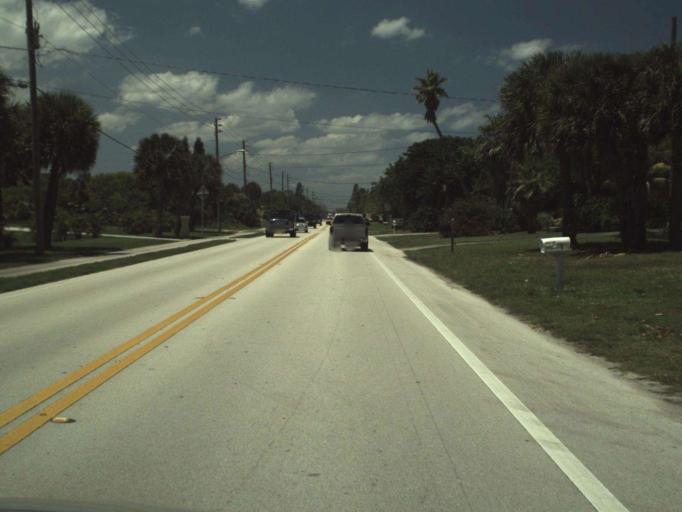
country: US
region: Florida
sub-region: Brevard County
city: Micco
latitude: 27.9459
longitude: -80.4965
